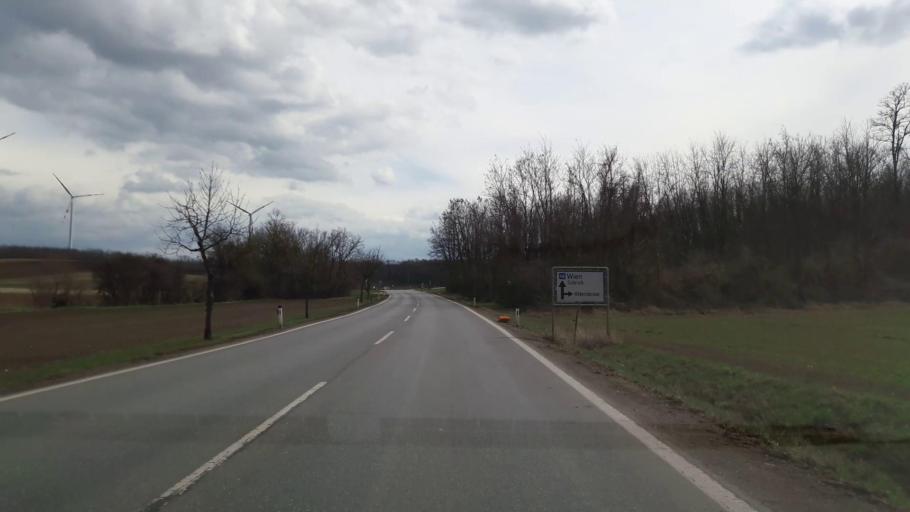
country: AT
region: Lower Austria
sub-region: Politischer Bezirk Mistelbach
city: Mistelbach
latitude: 48.5442
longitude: 16.5896
